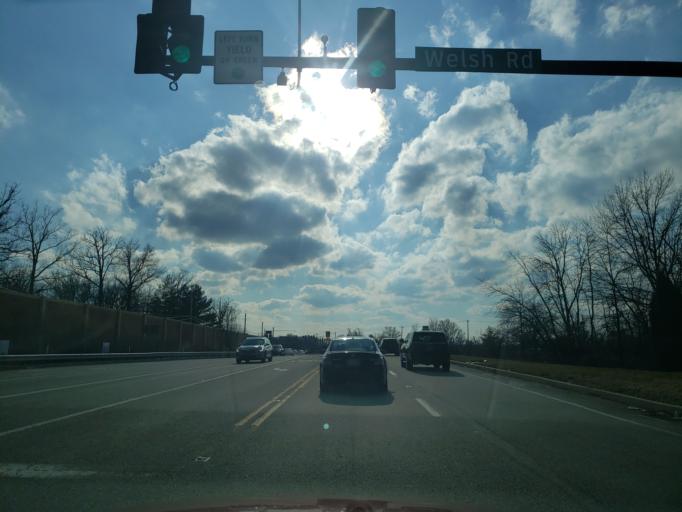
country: US
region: Pennsylvania
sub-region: Montgomery County
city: Montgomeryville
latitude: 40.2186
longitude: -75.2456
